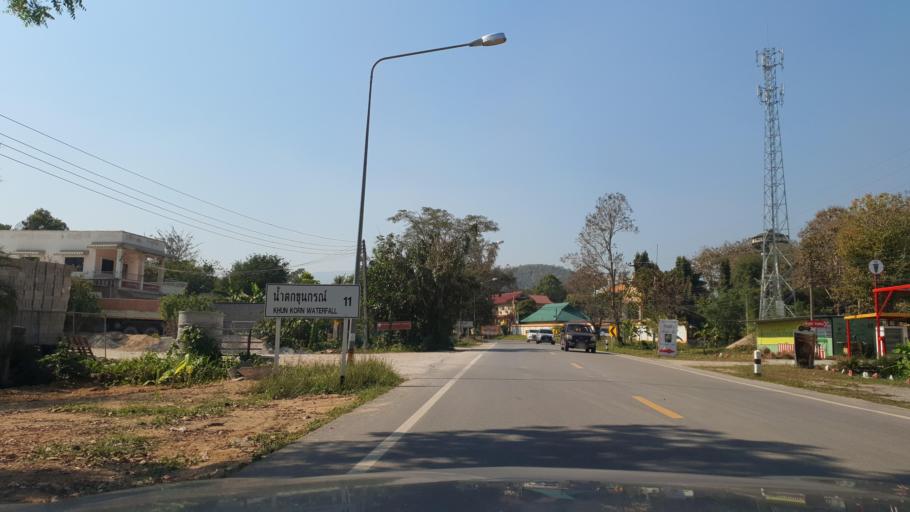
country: TH
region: Chiang Rai
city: Mae Lao
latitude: 19.8333
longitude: 99.7015
